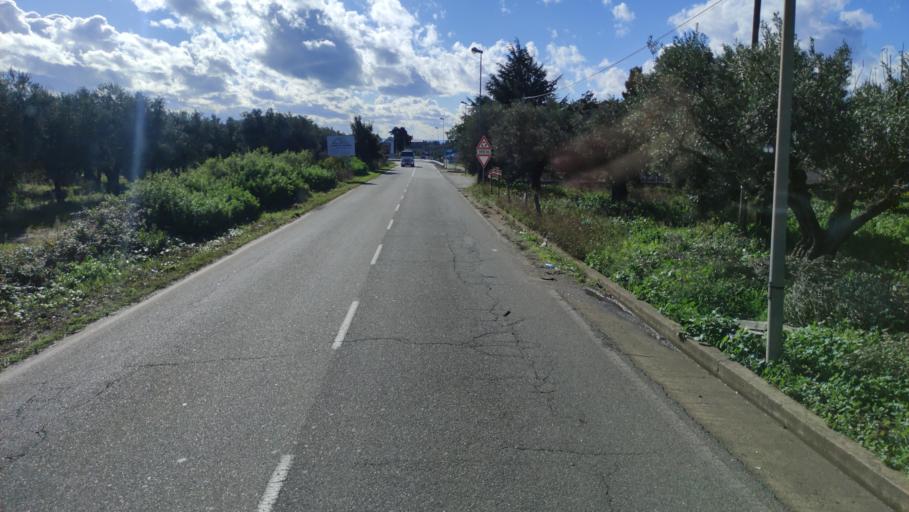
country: IT
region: Calabria
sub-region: Provincia di Catanzaro
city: Santa Eufemia Lamezia
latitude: 38.9265
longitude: 16.2843
